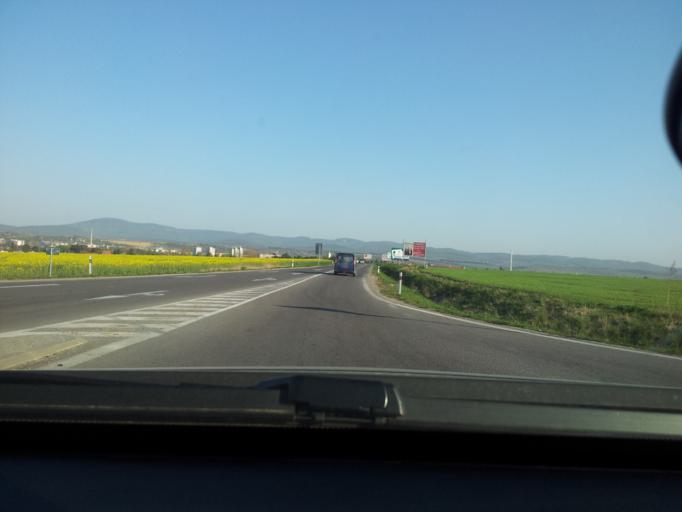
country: SK
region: Nitriansky
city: Zlate Moravce
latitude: 48.3741
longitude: 18.4051
